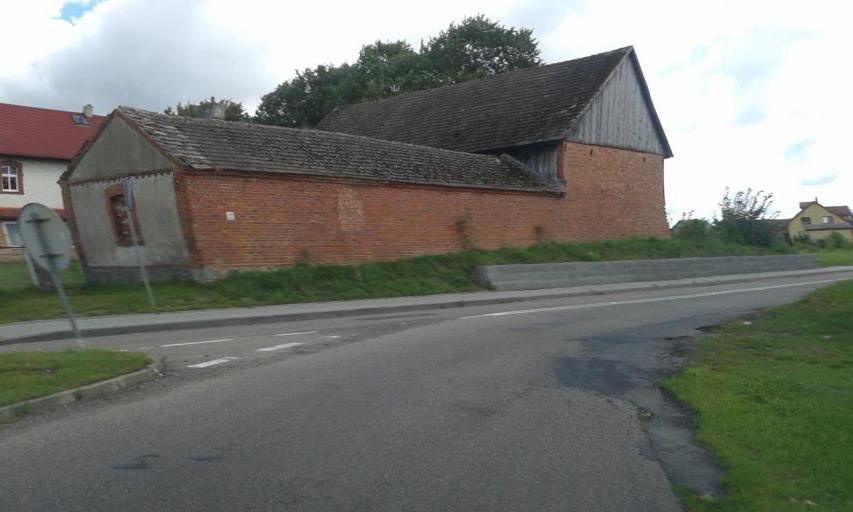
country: PL
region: West Pomeranian Voivodeship
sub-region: Powiat koszalinski
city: Bobolice
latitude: 53.9911
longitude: 16.6874
